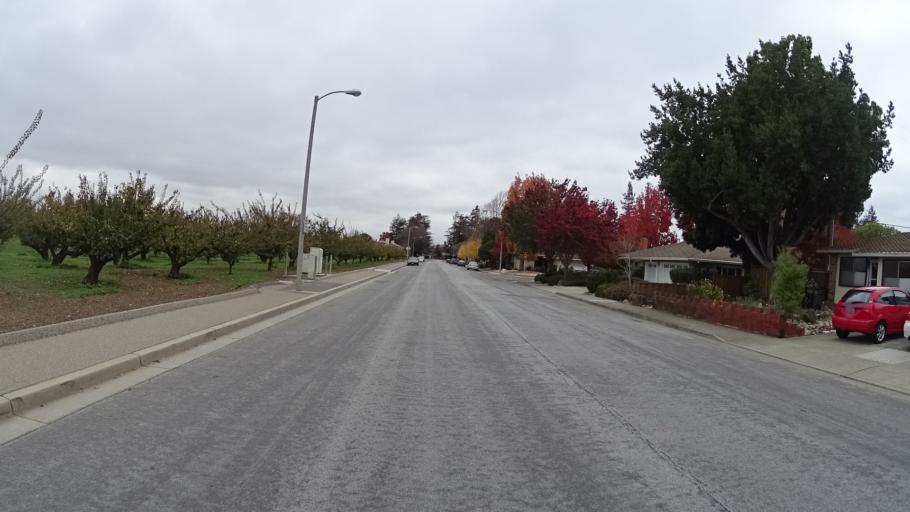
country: US
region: California
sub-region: Santa Clara County
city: Sunnyvale
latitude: 37.3554
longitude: -122.0269
